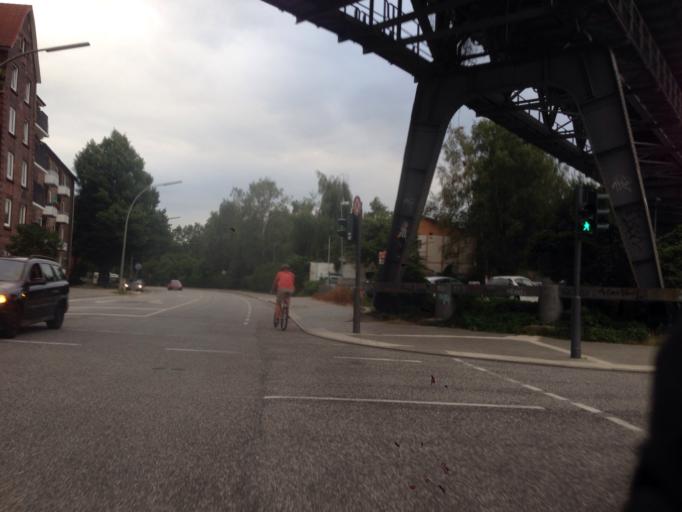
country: DE
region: Hamburg
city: Barmbek-Nord
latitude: 53.5915
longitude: 10.0386
